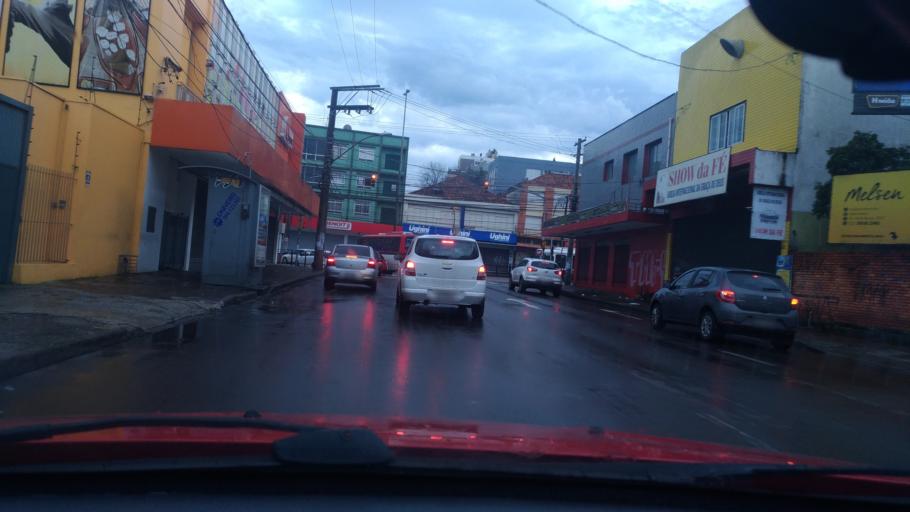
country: BR
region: Rio Grande do Sul
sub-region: Porto Alegre
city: Porto Alegre
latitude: -30.0115
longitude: -51.1620
